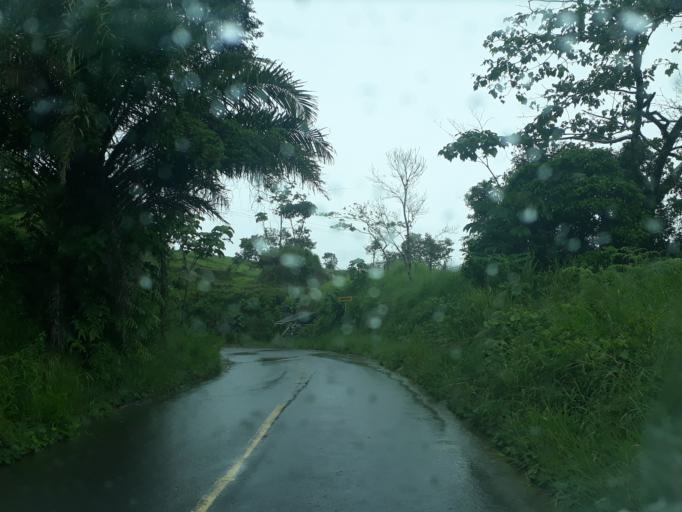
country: CO
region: Cundinamarca
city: Paratebueno
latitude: 4.3981
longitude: -73.3023
